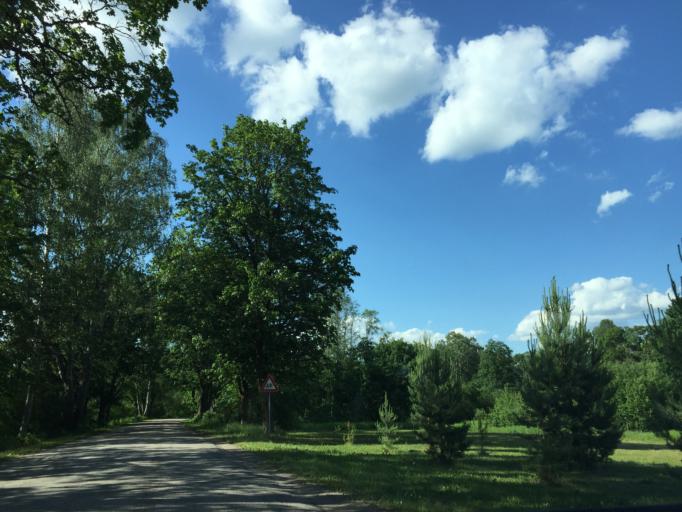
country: LV
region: Jaunpils
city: Jaunpils
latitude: 56.8783
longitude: 22.9913
